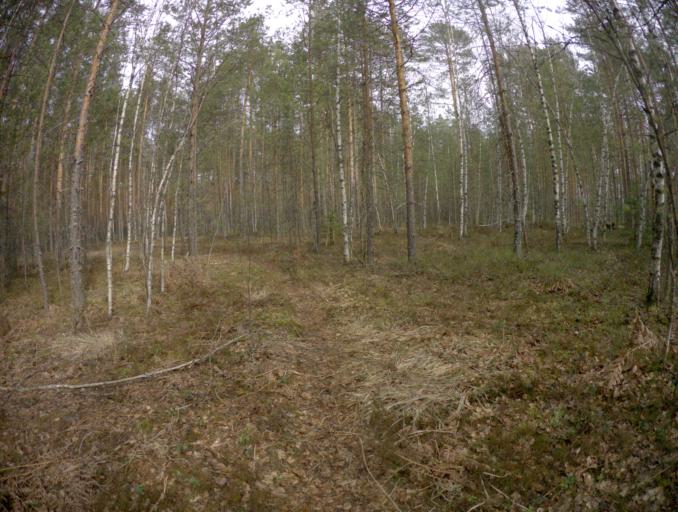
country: RU
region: Vladimir
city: Raduzhnyy
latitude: 55.9446
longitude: 40.2874
